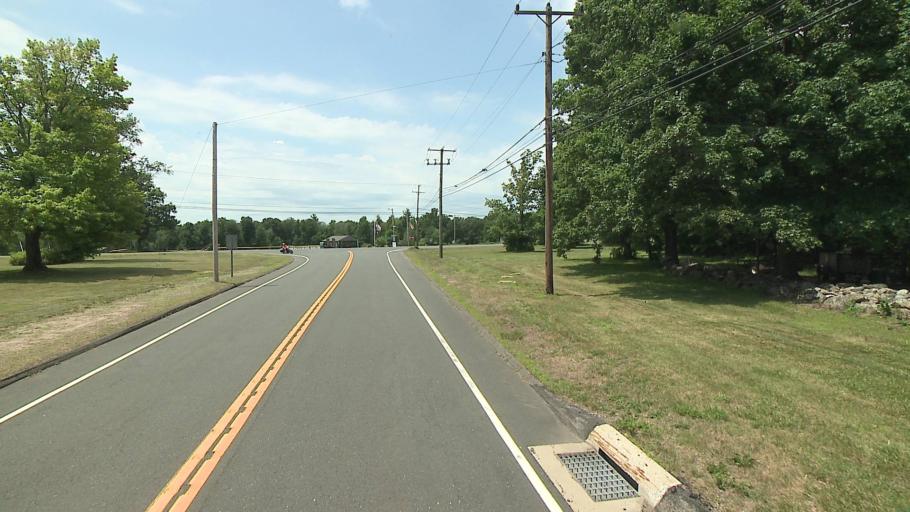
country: US
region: Connecticut
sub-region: Hartford County
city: North Granby
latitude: 41.9948
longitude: -72.8993
